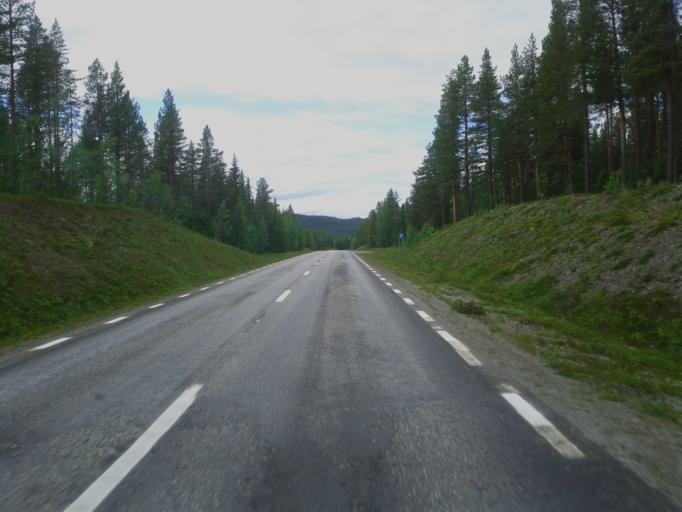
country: SE
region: Vaesterbotten
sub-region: Storumans Kommun
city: Fristad
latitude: 65.3582
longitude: 16.5484
